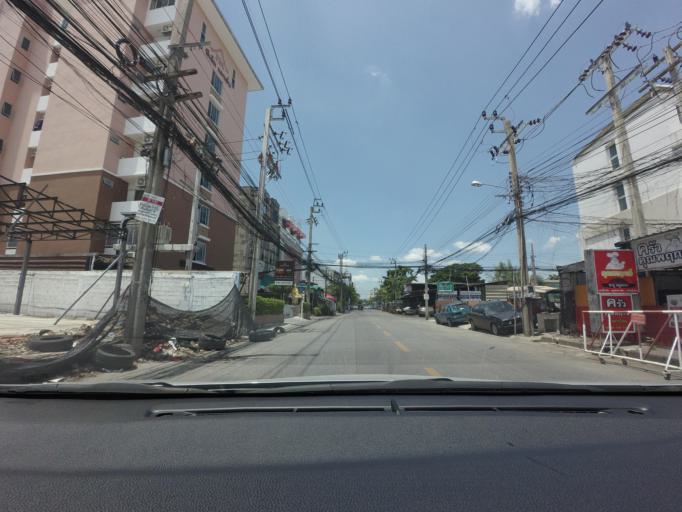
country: TH
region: Bangkok
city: Bang Na
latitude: 13.6975
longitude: 100.6378
